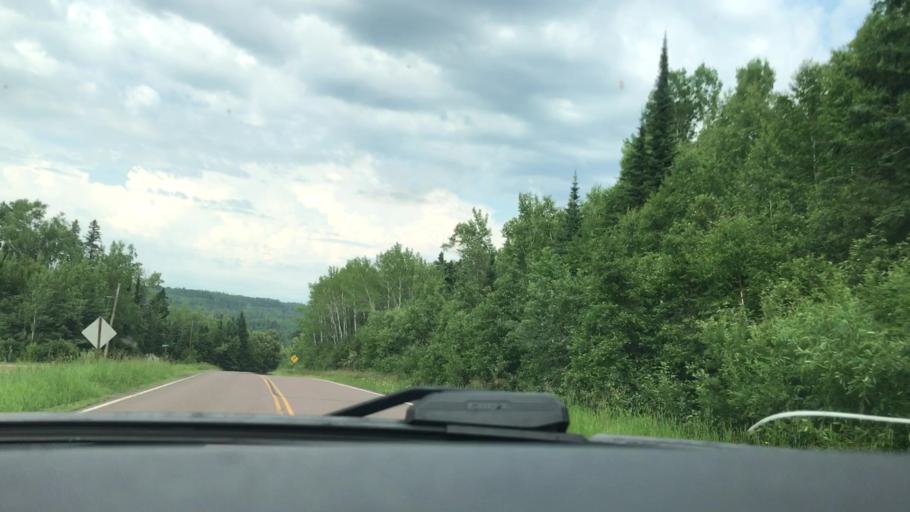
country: CA
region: Ontario
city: Neebing
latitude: 47.9626
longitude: -89.6923
